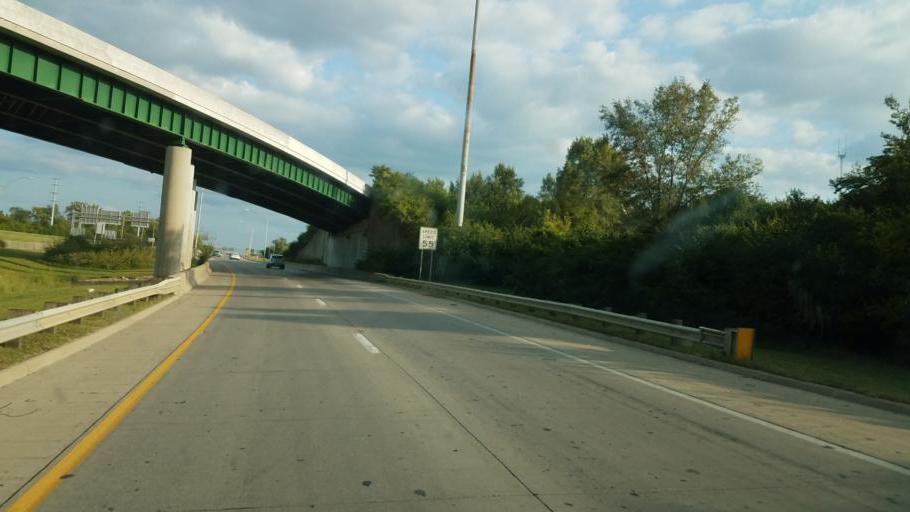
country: US
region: Ohio
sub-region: Franklin County
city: Columbus
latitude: 39.9497
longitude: -83.0169
